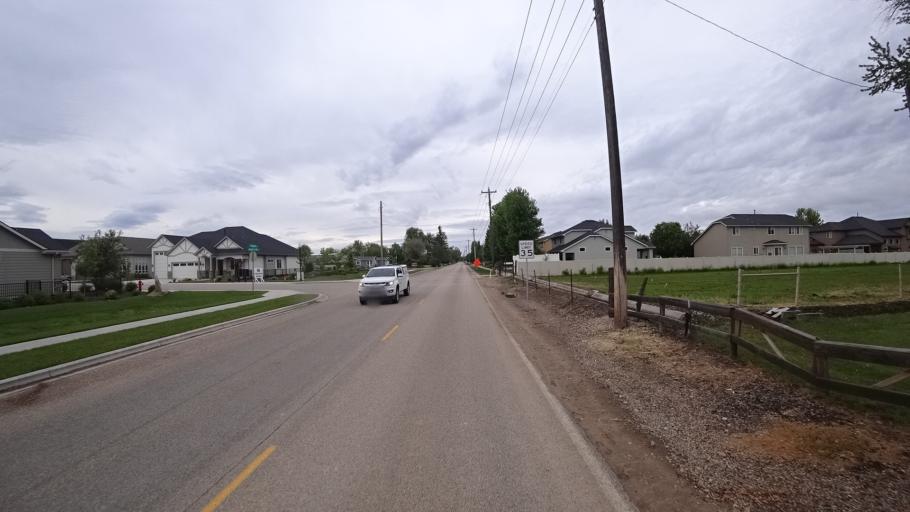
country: US
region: Idaho
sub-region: Ada County
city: Star
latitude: 43.6989
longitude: -116.4733
